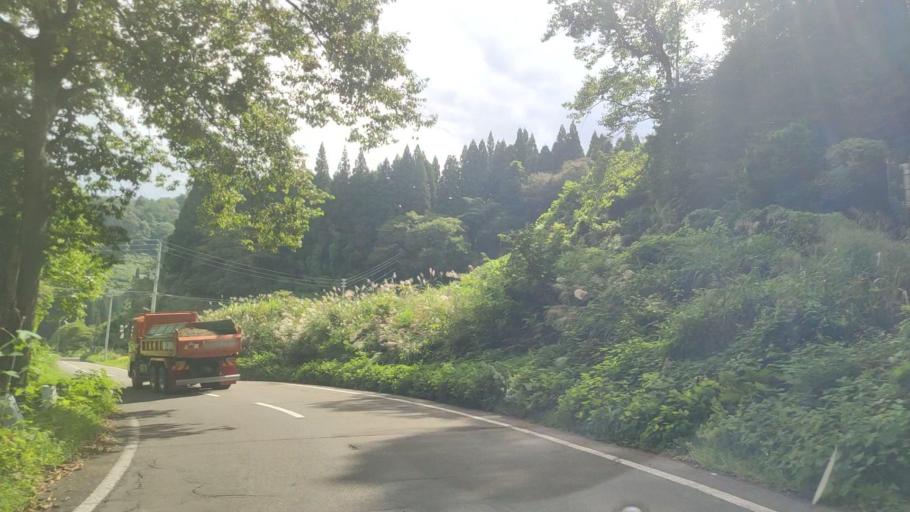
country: JP
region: Niigata
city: Arai
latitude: 36.9458
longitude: 138.2879
